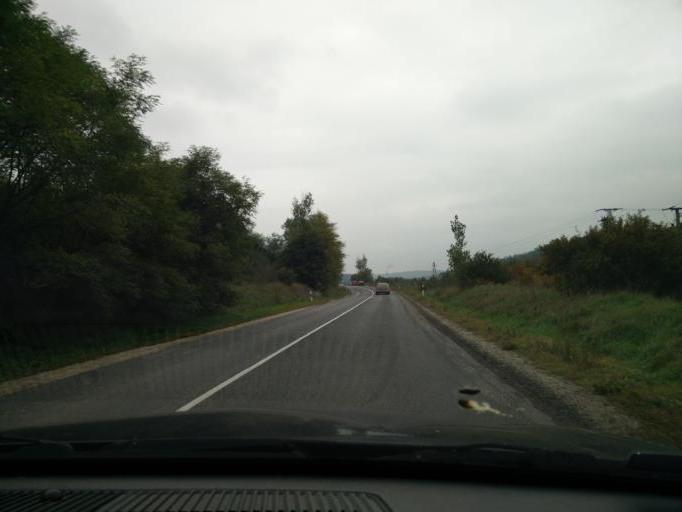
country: HU
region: Komarom-Esztergom
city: Piliscsev
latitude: 47.6657
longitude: 18.7813
